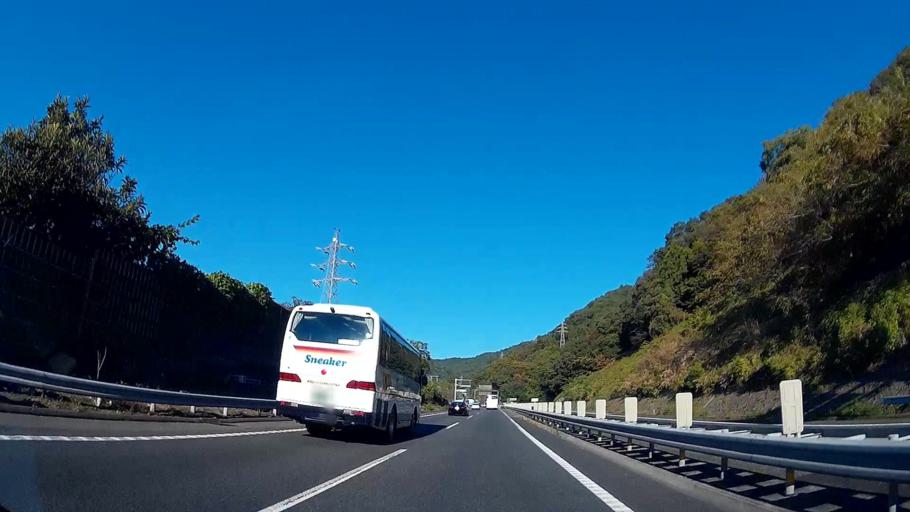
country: JP
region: Yamanashi
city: Uenohara
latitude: 35.6193
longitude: 139.1827
